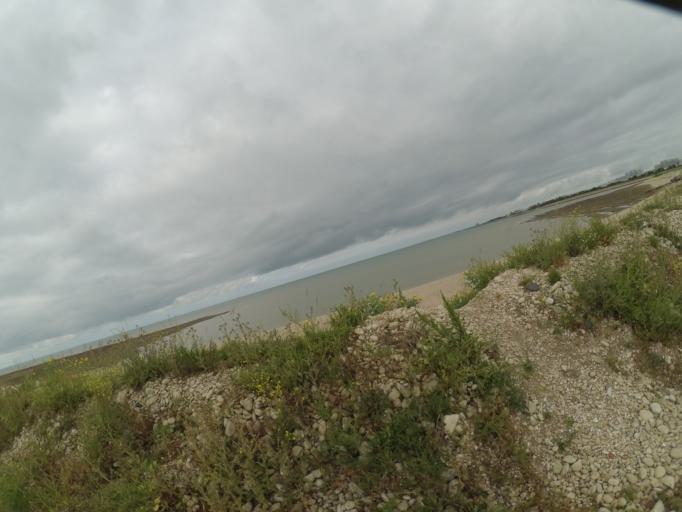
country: FR
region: Poitou-Charentes
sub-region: Departement de la Charente-Maritime
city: Aytre
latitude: 46.1322
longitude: -1.1484
